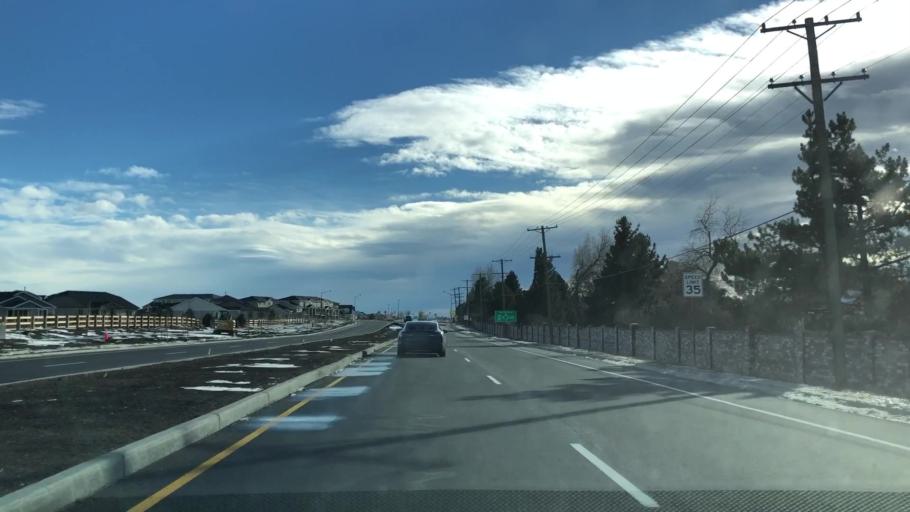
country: US
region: Colorado
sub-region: Larimer County
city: Loveland
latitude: 40.4223
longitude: -105.0209
